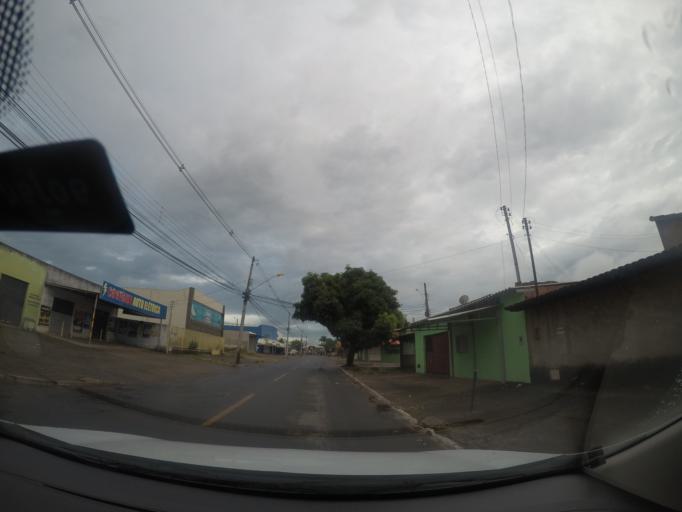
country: BR
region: Goias
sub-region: Goiania
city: Goiania
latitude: -16.6992
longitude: -49.3501
